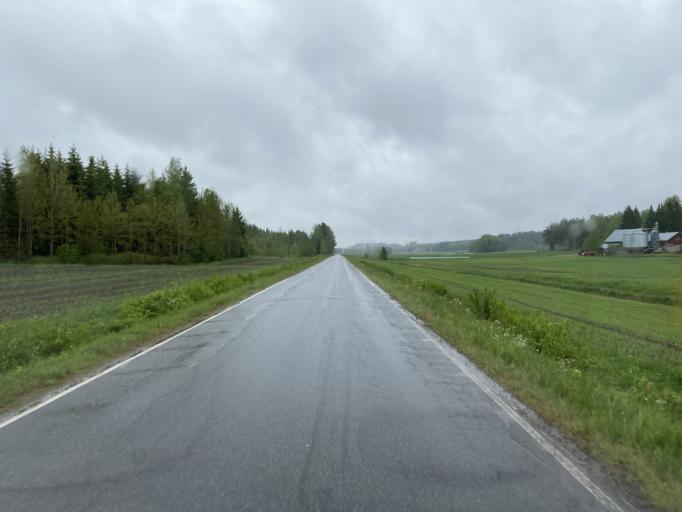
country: FI
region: Haeme
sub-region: Forssa
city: Humppila
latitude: 61.0457
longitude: 23.3782
